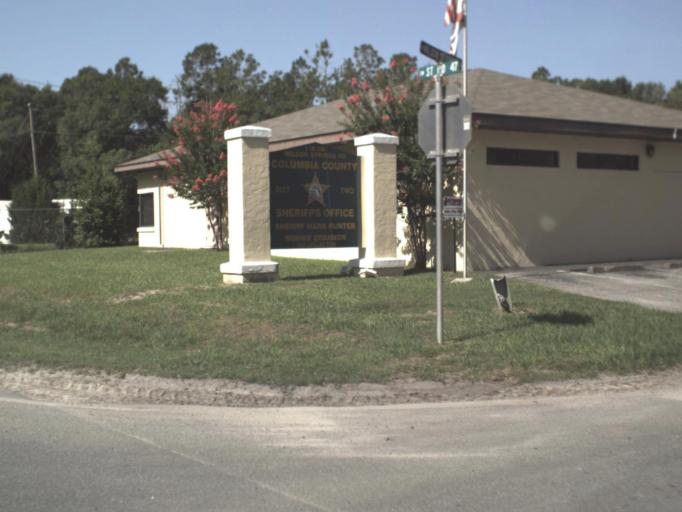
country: US
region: Florida
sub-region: Alachua County
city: High Springs
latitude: 29.9216
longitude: -82.7139
